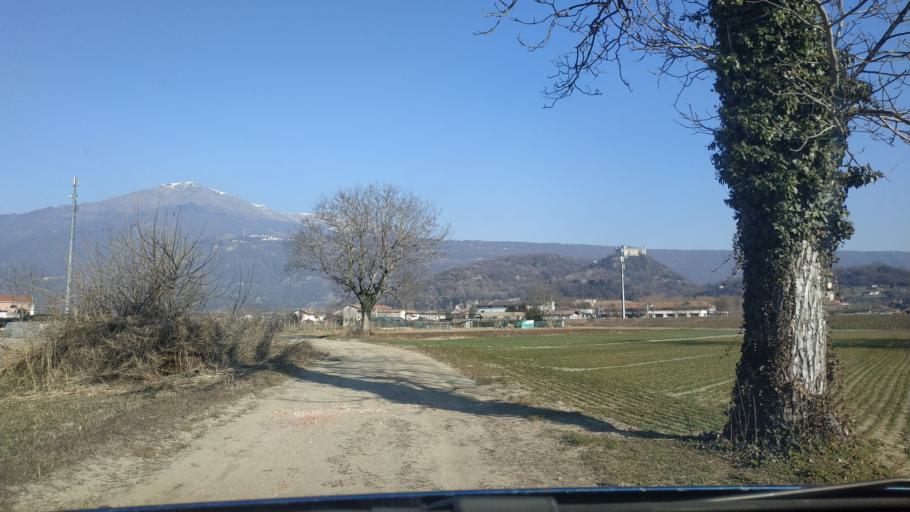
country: IT
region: Piedmont
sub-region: Provincia di Torino
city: Montalto Dora
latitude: 45.4889
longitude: 7.8552
